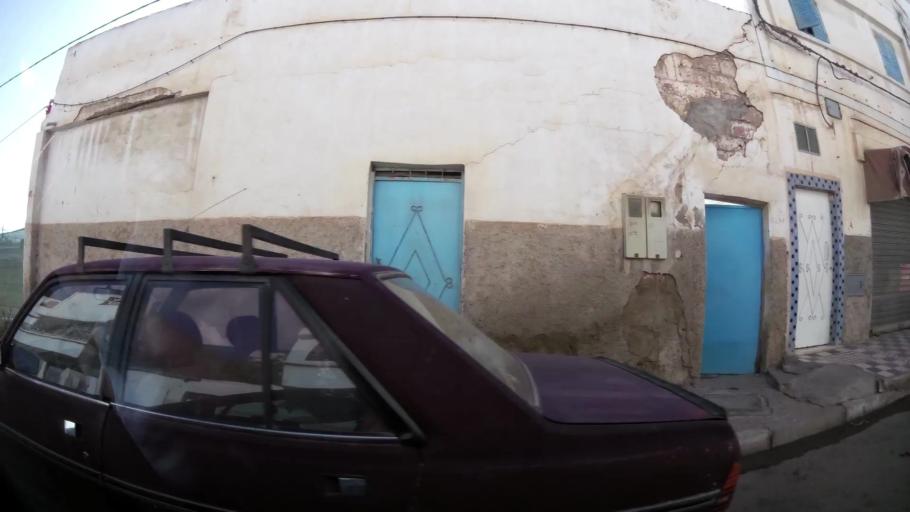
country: MA
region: Souss-Massa-Draa
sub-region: Inezgane-Ait Mellou
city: Inezgane
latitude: 30.3714
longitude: -9.5030
